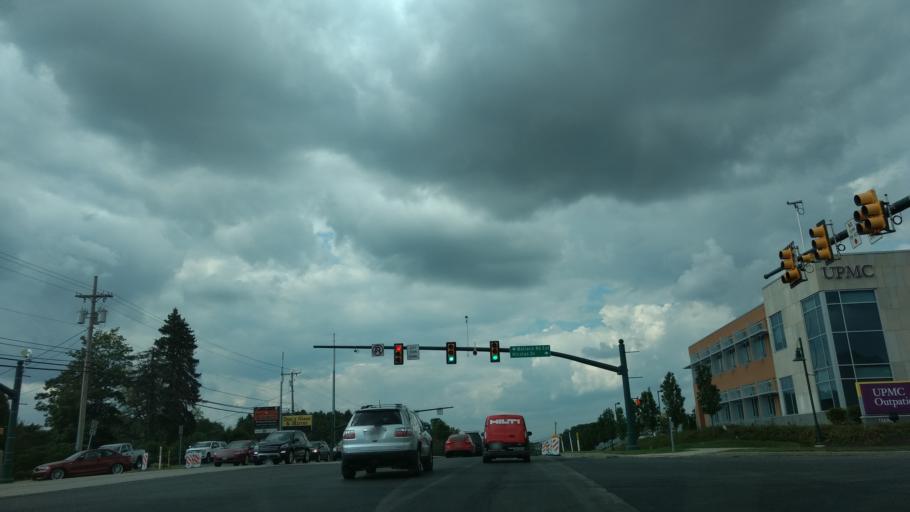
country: US
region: Pennsylvania
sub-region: Allegheny County
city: Bradford Woods
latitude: 40.6379
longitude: -80.0634
